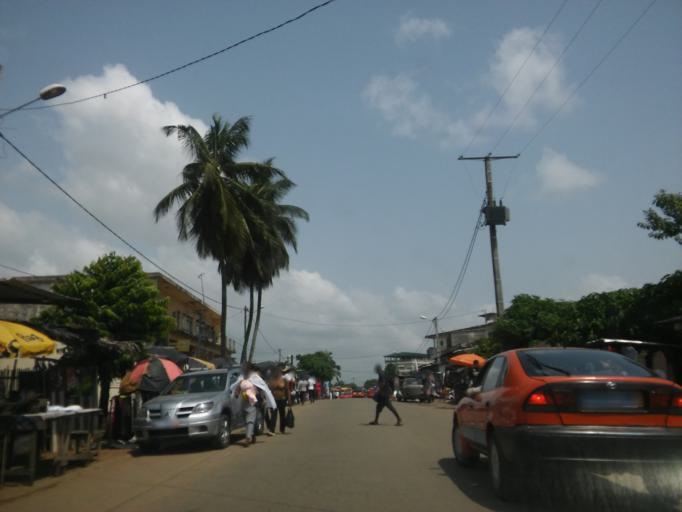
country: CI
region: Sud-Comoe
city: Grand-Bassam
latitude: 5.2166
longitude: -3.7361
